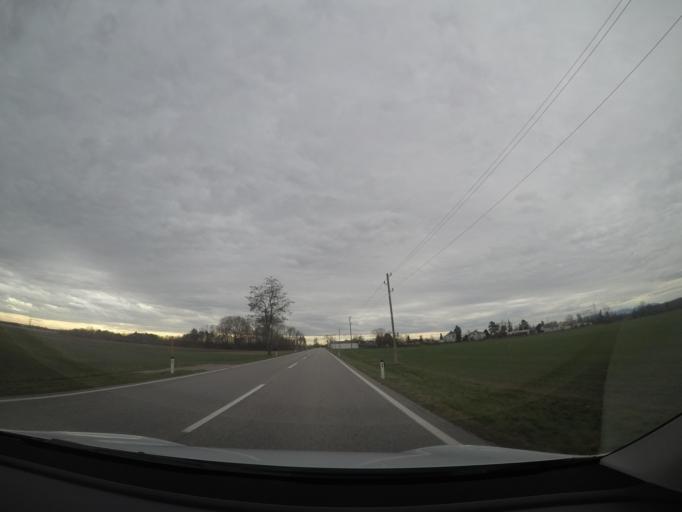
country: AT
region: Lower Austria
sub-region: Politischer Bezirk Modling
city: Achau
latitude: 48.0622
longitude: 16.3822
